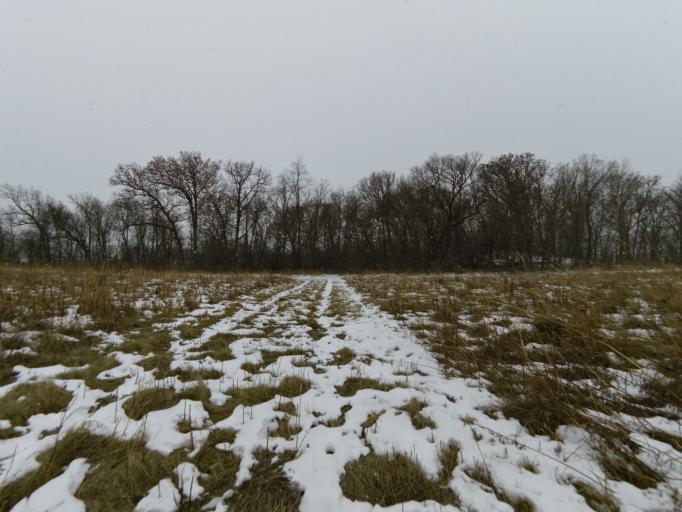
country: US
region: Minnesota
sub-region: Washington County
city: Lake Elmo
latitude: 44.9819
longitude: -92.9139
